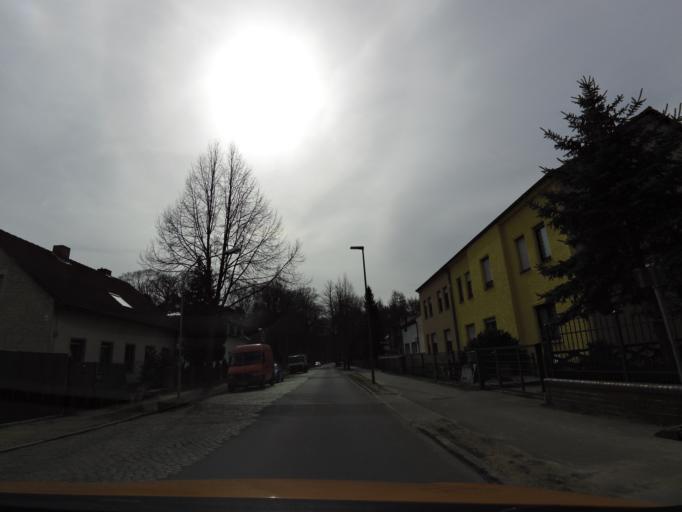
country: DE
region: Brandenburg
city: Rangsdorf
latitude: 52.3275
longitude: 13.3920
